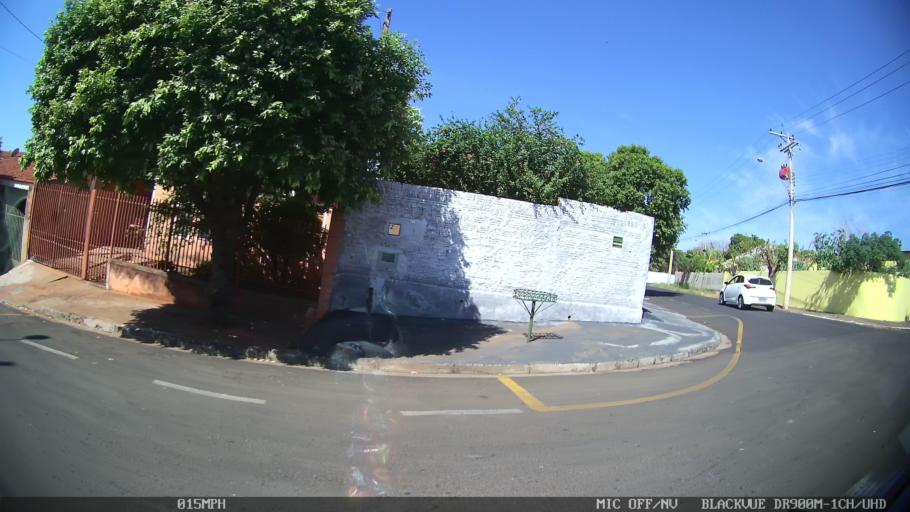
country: BR
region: Sao Paulo
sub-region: Sao Jose Do Rio Preto
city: Sao Jose do Rio Preto
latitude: -20.7756
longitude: -49.4026
